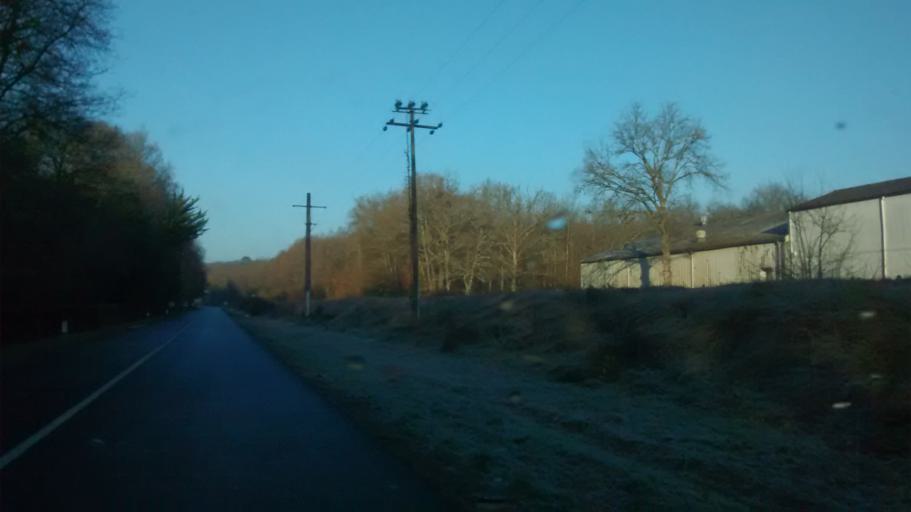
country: FR
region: Centre
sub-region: Departement d'Indre-et-Loire
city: Veigne
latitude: 47.2915
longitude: 0.7505
